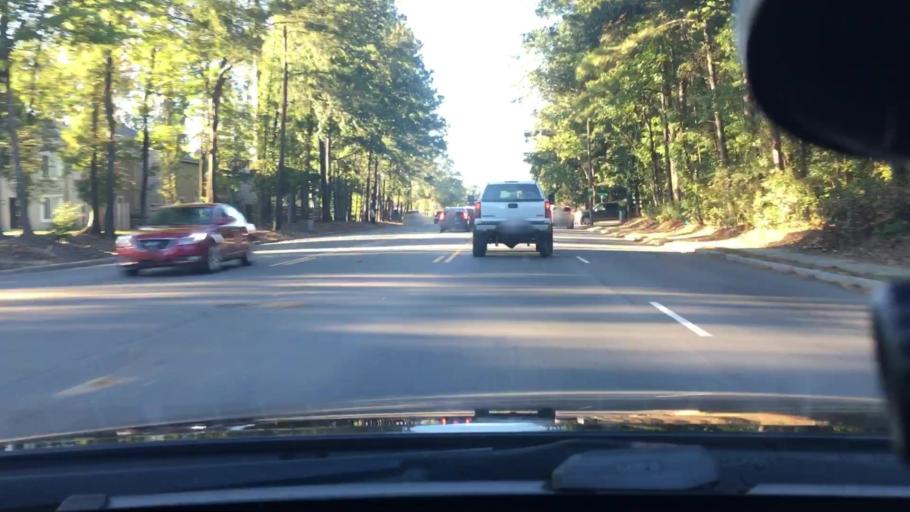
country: US
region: North Carolina
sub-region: Pitt County
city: Windsor
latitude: 35.5802
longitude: -77.3646
